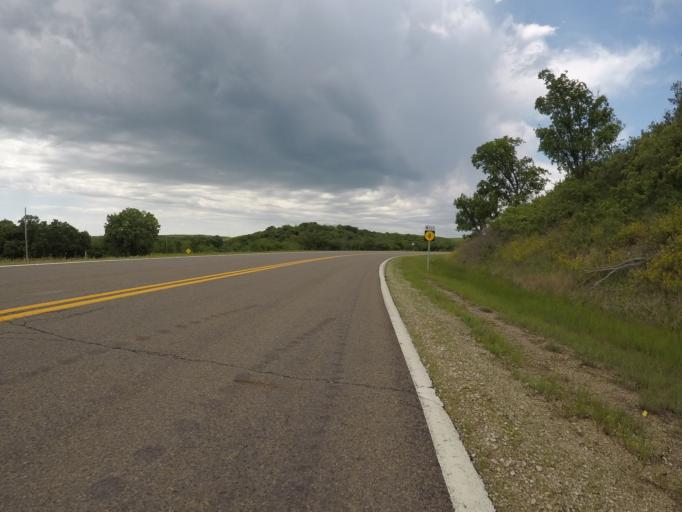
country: US
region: Kansas
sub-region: Wabaunsee County
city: Alma
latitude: 38.8684
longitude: -96.2943
